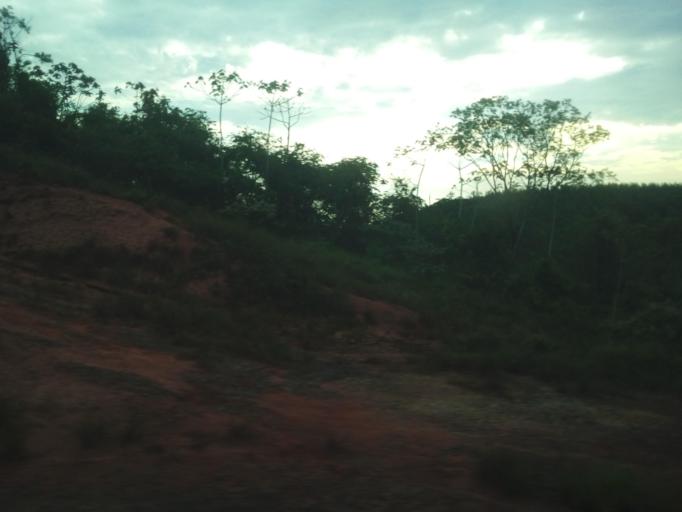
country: BR
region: Maranhao
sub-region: Imperatriz
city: Imperatriz
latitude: -4.7512
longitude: -47.3066
